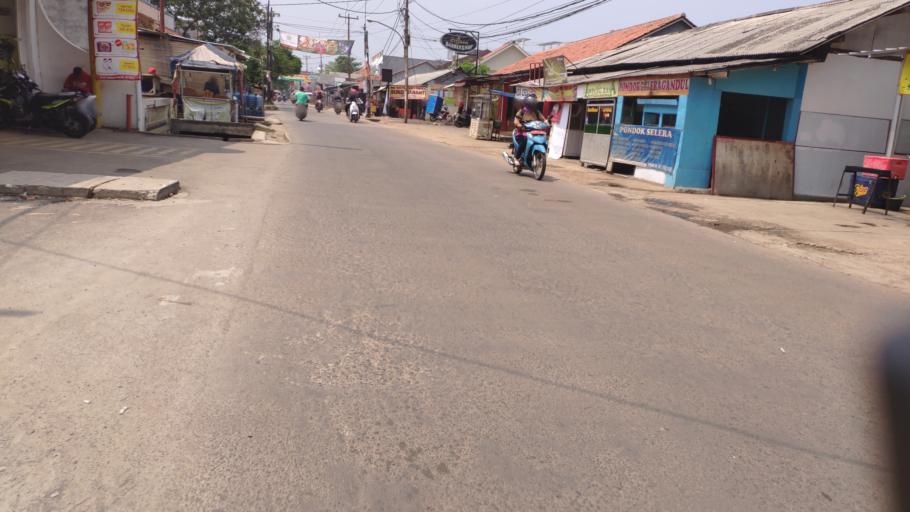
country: ID
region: West Java
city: Pamulang
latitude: -6.3409
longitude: 106.7928
